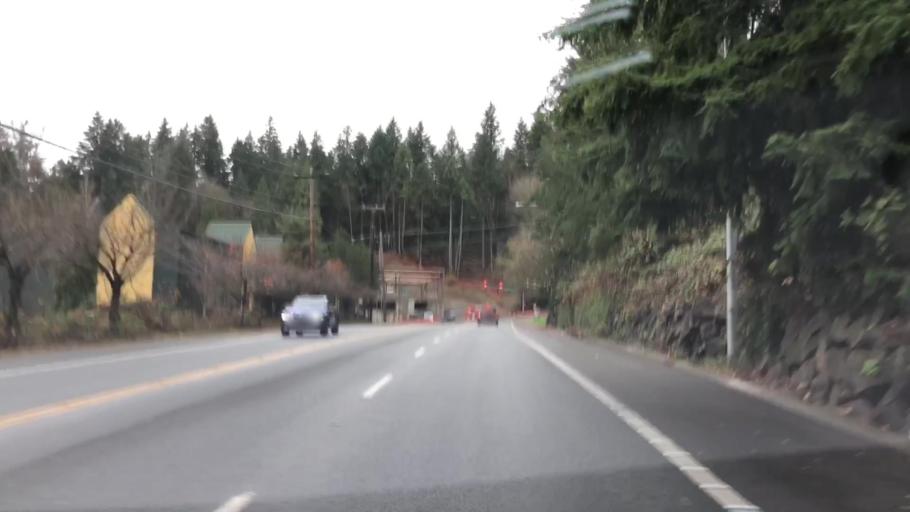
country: US
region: Washington
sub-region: King County
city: Woodinville
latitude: 47.7634
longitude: -122.1440
